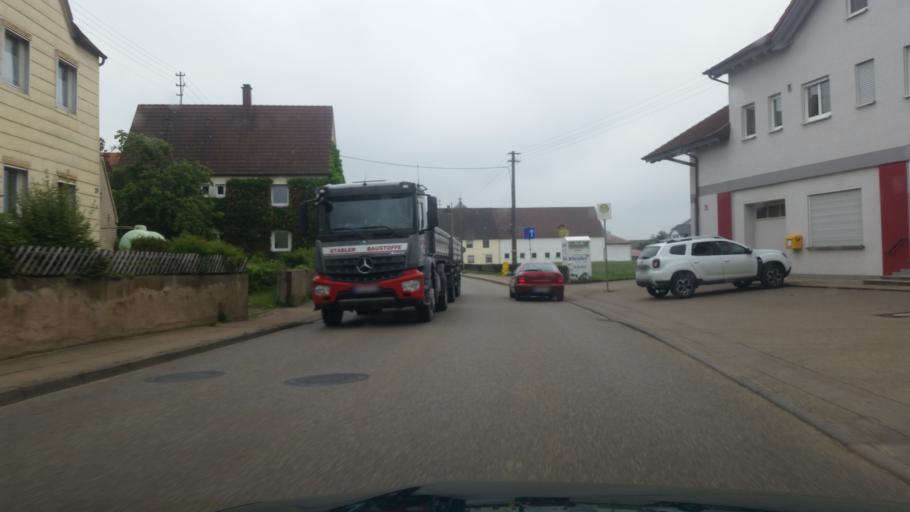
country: DE
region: Baden-Wuerttemberg
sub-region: Regierungsbezirk Stuttgart
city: Kirchheim am Ries
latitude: 48.8437
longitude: 10.3945
